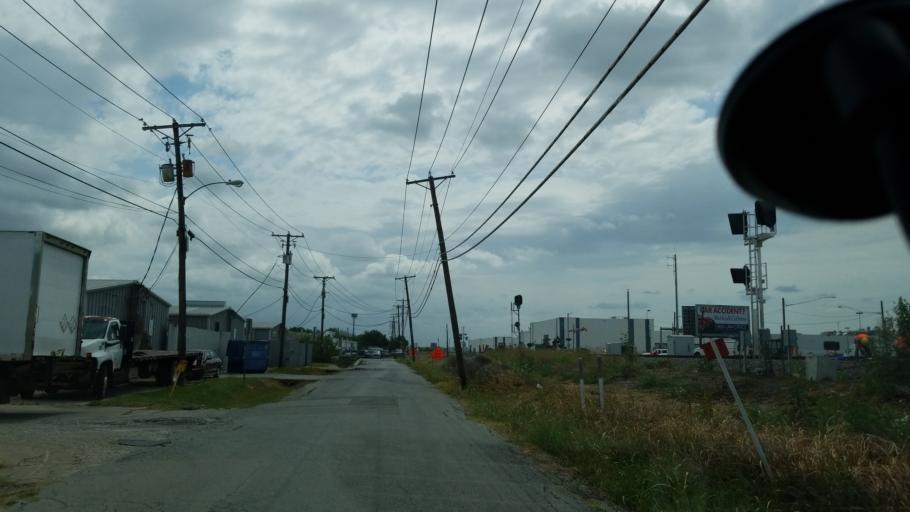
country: US
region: Texas
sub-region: Dallas County
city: Grand Prairie
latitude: 32.7456
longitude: -96.9890
